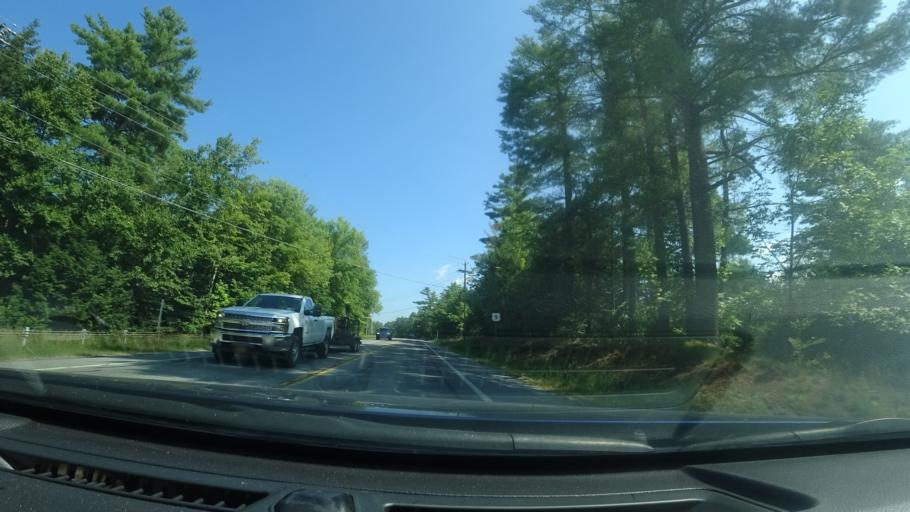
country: US
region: New York
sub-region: Warren County
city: Warrensburg
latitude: 43.6349
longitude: -73.7981
